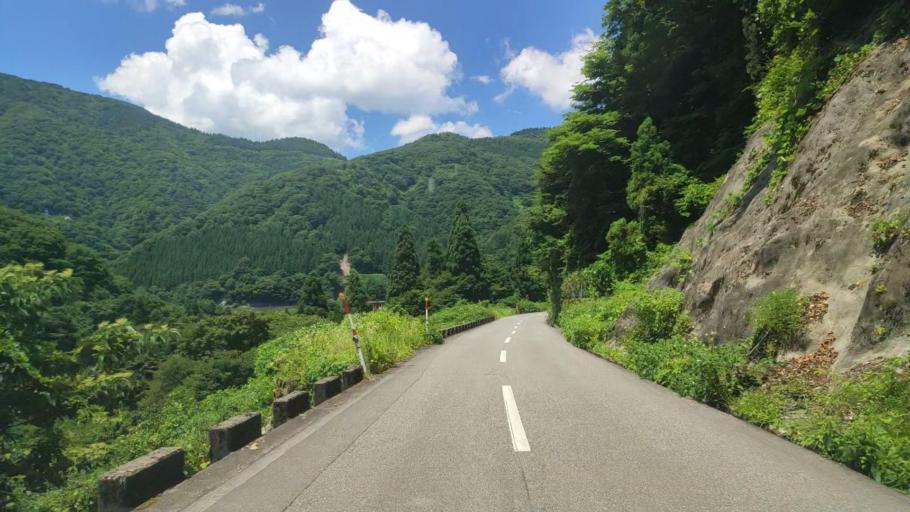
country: JP
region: Fukui
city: Ono
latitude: 35.8977
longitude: 136.5189
